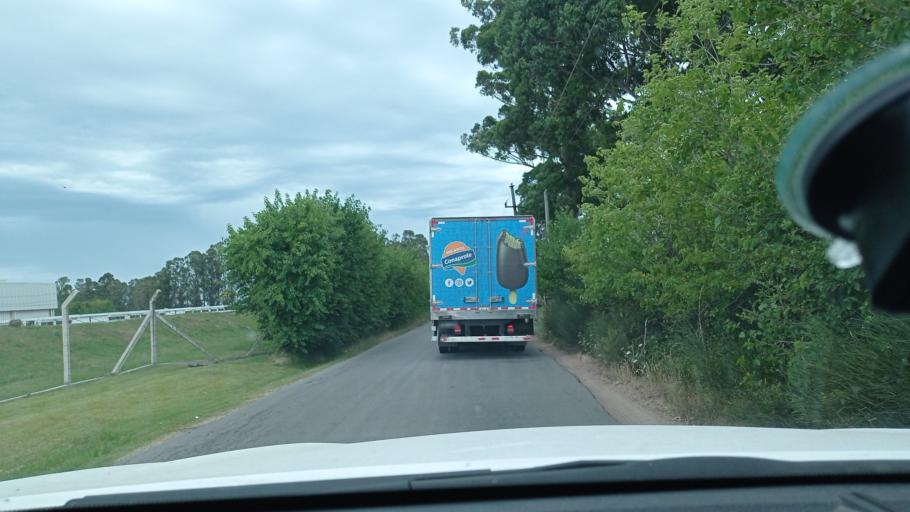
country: UY
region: Canelones
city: La Paz
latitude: -34.8059
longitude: -56.1881
